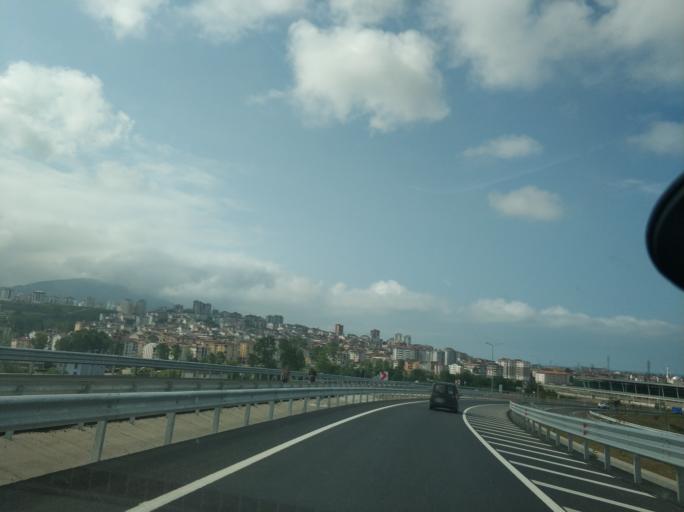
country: TR
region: Ordu
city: Ordu
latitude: 40.9545
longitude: 37.9027
